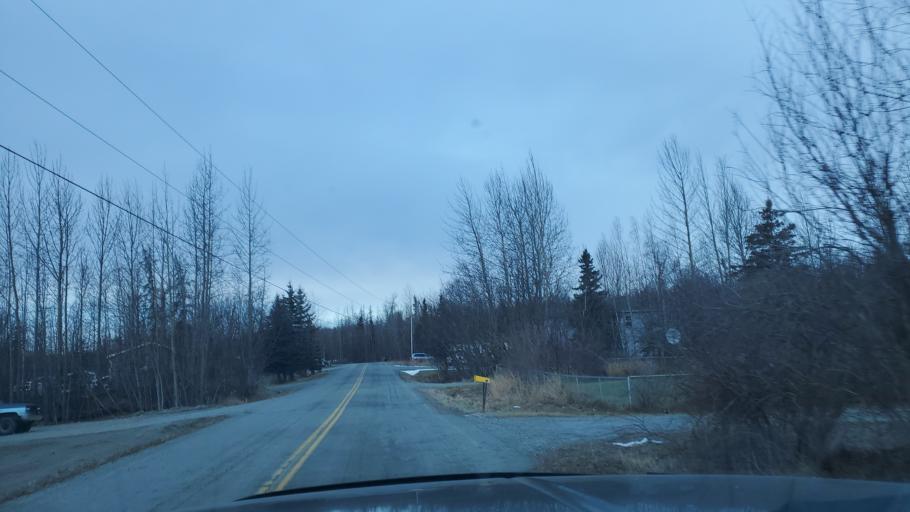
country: US
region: Alaska
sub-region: Matanuska-Susitna Borough
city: Lakes
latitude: 61.5725
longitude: -149.3353
